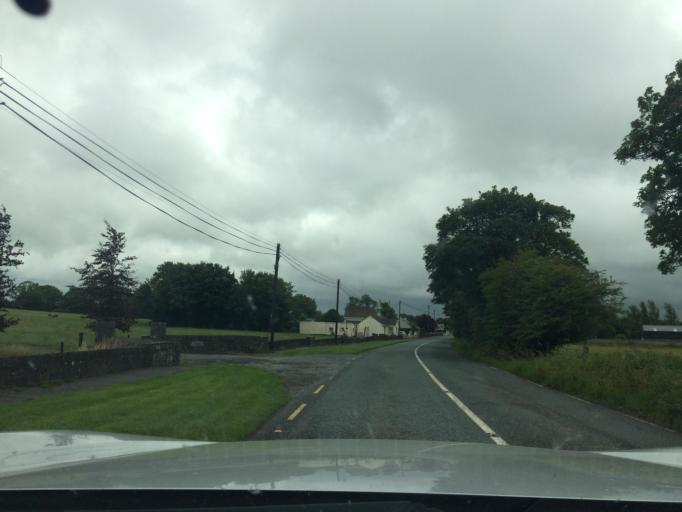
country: IE
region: Munster
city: Cashel
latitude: 52.5058
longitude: -7.8718
